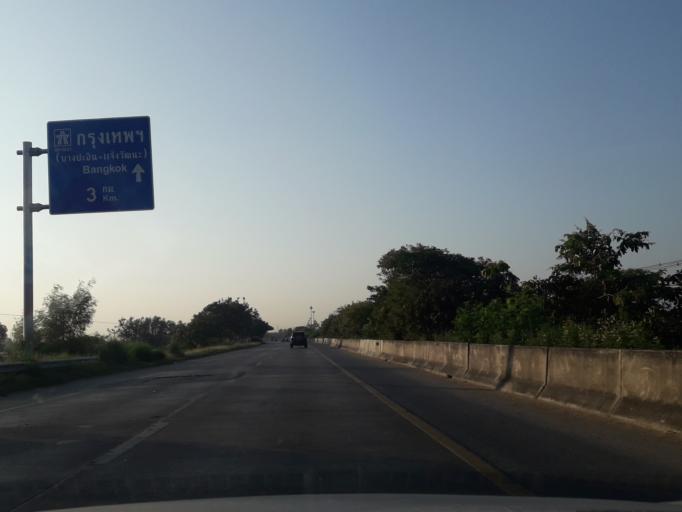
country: TH
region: Phra Nakhon Si Ayutthaya
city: Bang Pa-in
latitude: 14.1729
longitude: 100.5613
